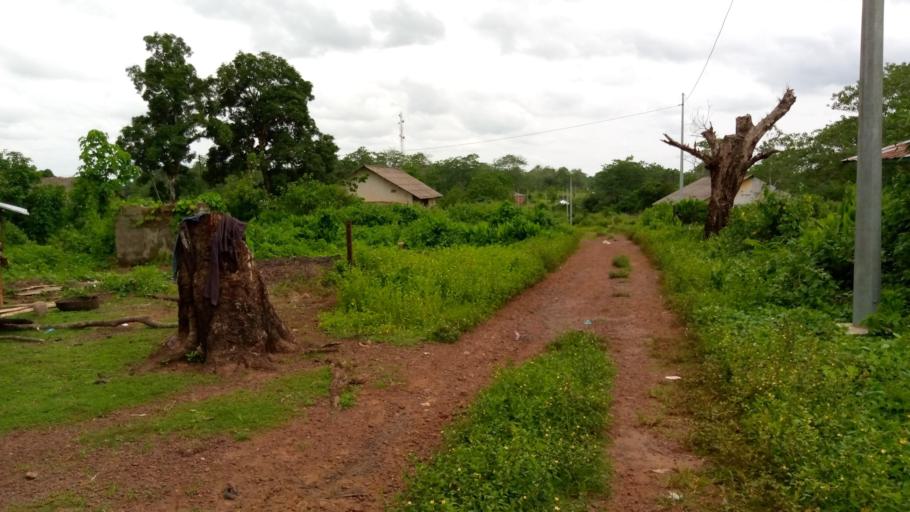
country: SL
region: Southern Province
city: Rotifunk
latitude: 8.1920
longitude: -12.5670
